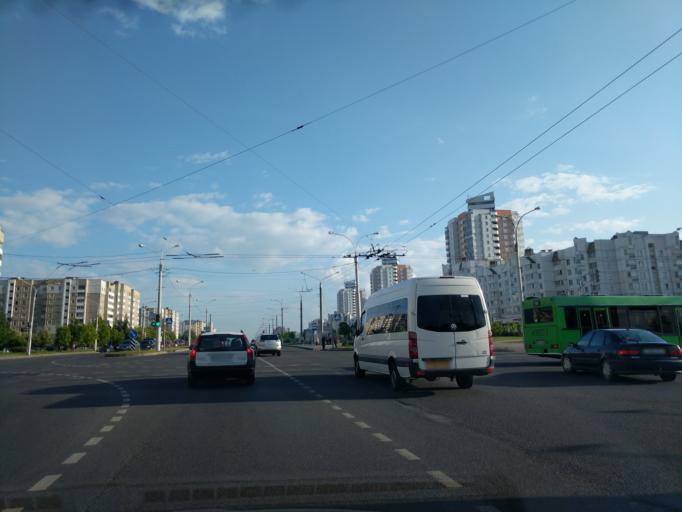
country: BY
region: Minsk
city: Zhdanovichy
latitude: 53.9164
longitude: 27.4368
